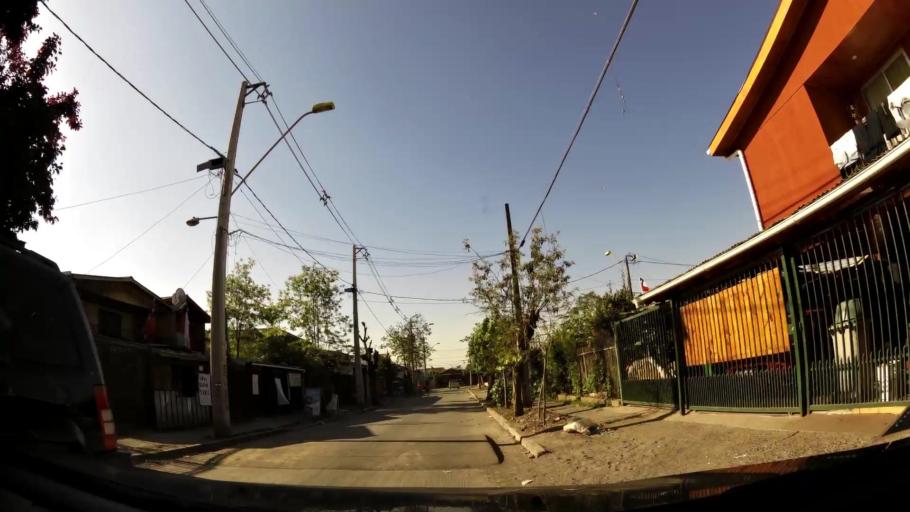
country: CL
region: Santiago Metropolitan
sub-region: Provincia de Santiago
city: La Pintana
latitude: -33.5775
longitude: -70.6554
